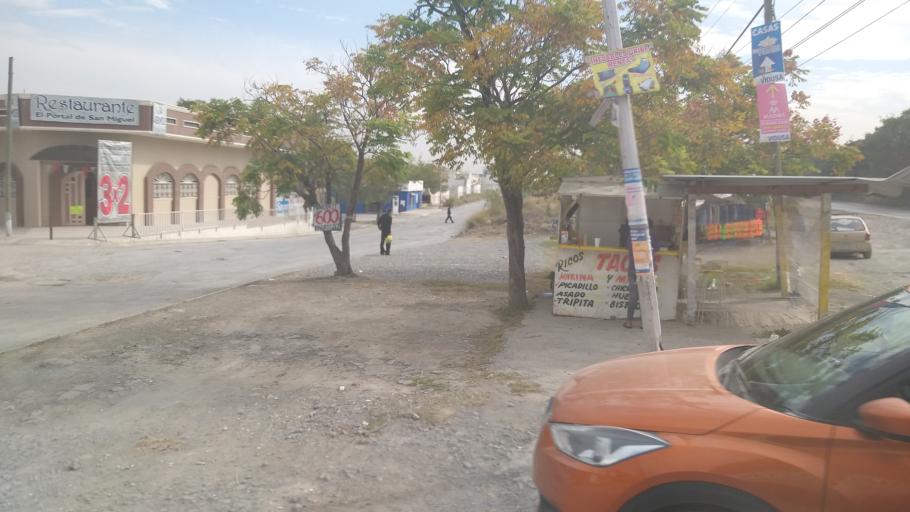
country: MX
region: Nuevo Leon
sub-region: Apodaca
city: Loma la Paz
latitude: 25.7026
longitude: -100.1459
